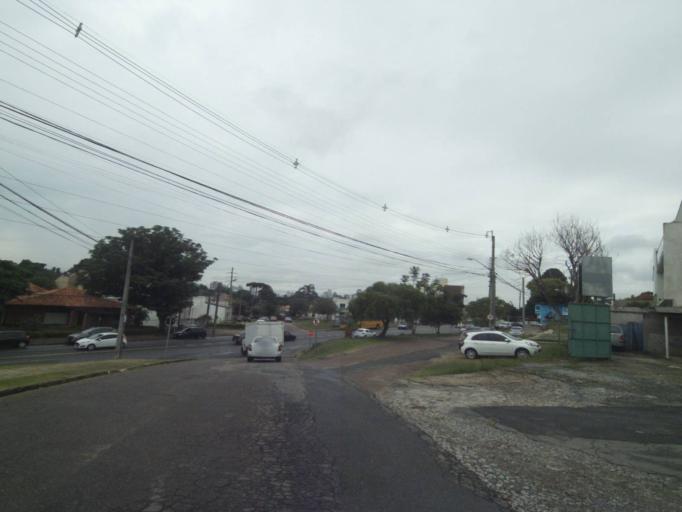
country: BR
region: Parana
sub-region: Curitiba
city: Curitiba
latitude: -25.4094
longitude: -49.2827
